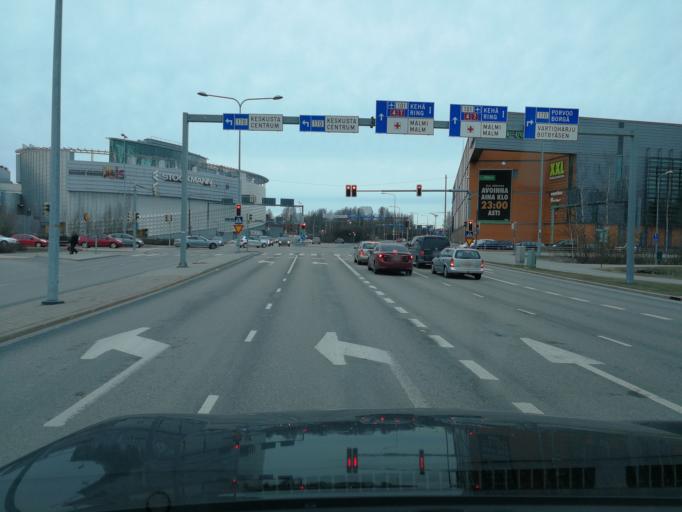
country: FI
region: Uusimaa
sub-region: Helsinki
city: Vantaa
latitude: 60.2118
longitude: 25.0883
